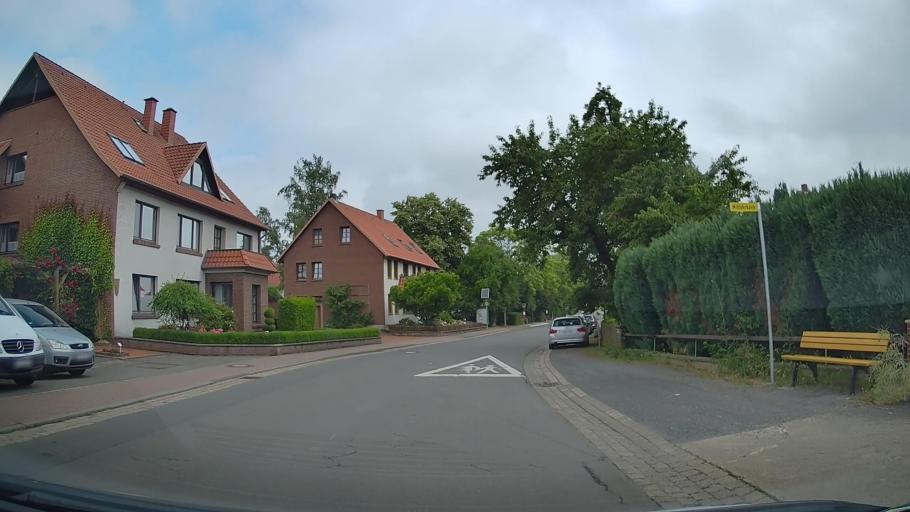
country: DE
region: Lower Saxony
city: Rinteln
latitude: 52.1645
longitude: 9.0308
